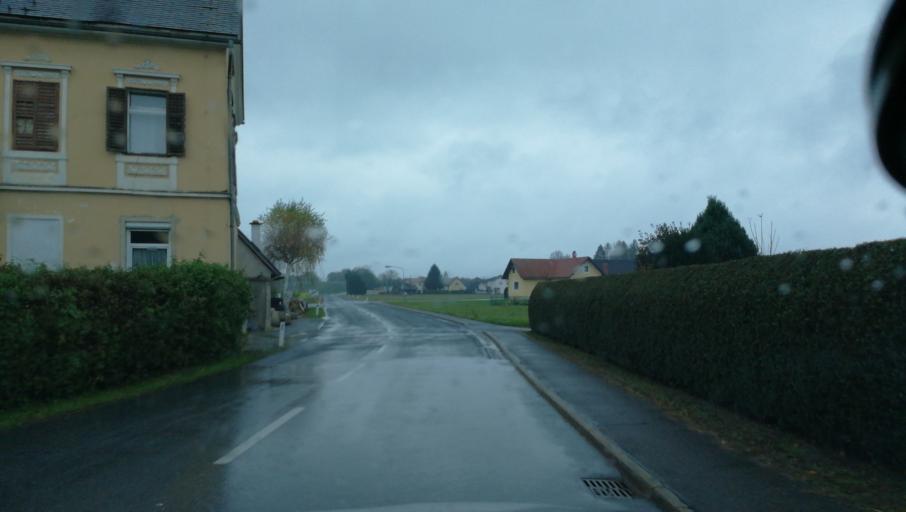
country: AT
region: Styria
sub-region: Politischer Bezirk Leibnitz
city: Sankt Veit am Vogau
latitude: 46.7451
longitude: 15.6235
